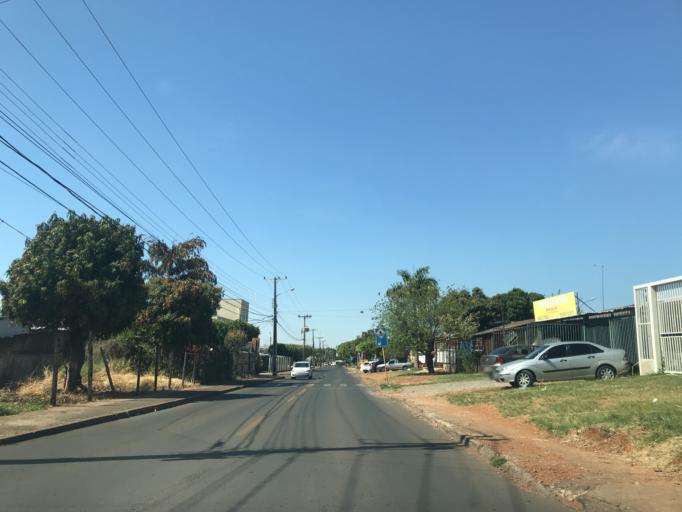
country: BR
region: Federal District
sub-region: Brasilia
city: Brasilia
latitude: -15.8138
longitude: -48.0814
